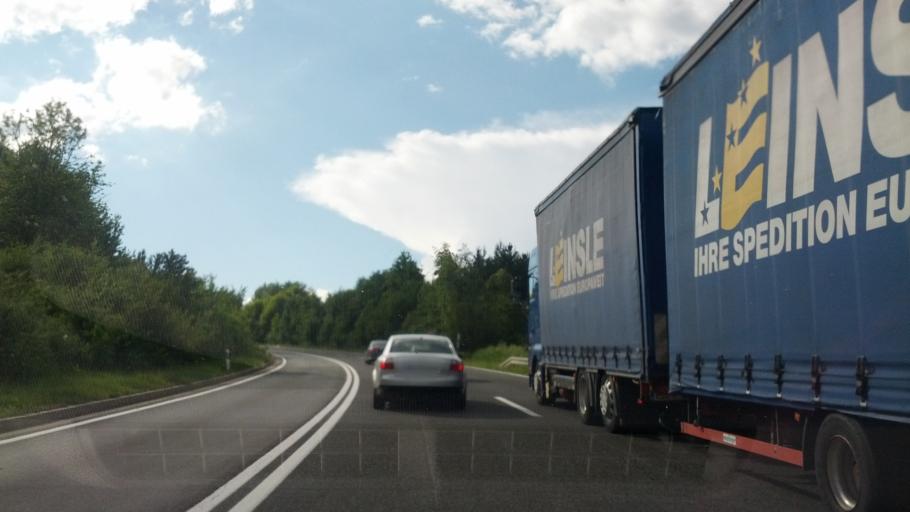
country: HR
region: Karlovacka
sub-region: Grad Karlovac
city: Slunj
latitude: 45.0596
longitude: 15.6186
